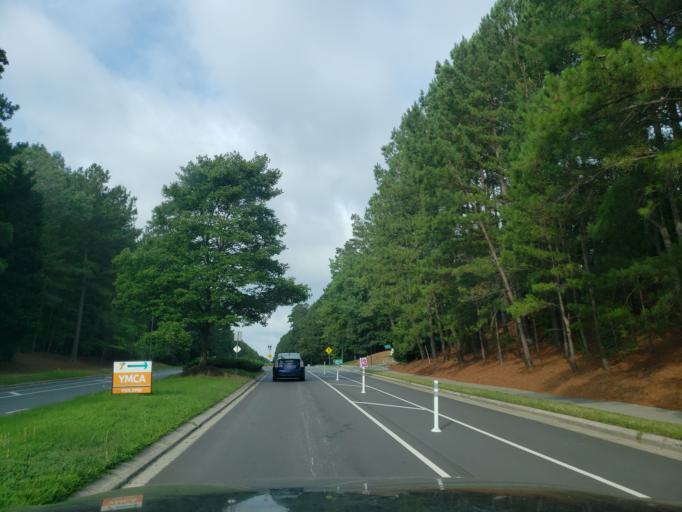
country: US
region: North Carolina
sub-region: Durham County
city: Durham
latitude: 35.9338
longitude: -78.9365
